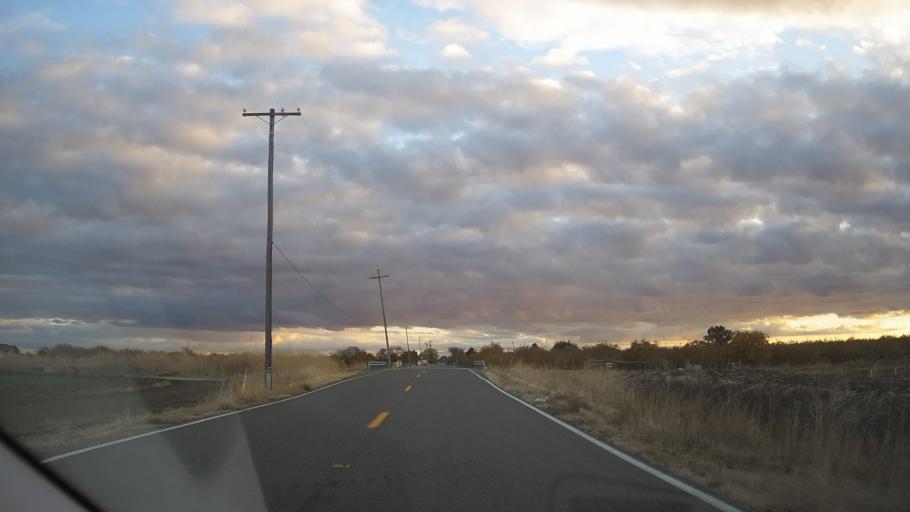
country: US
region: California
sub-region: Solano County
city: Hartley
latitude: 38.3742
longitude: -121.9061
